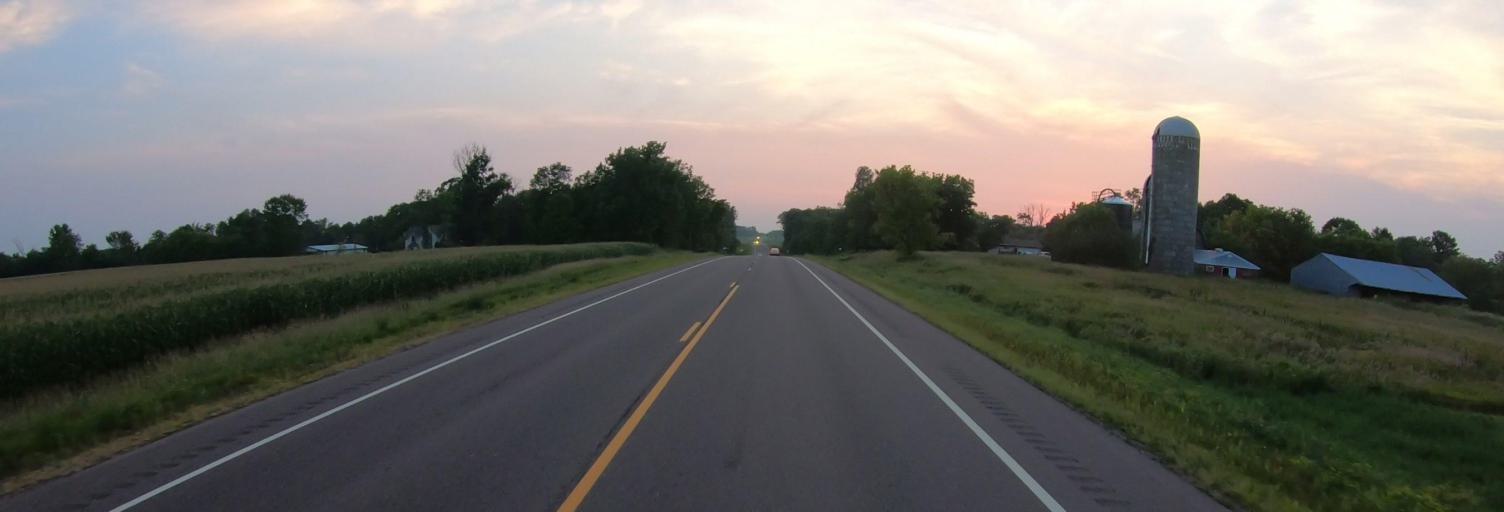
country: US
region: Minnesota
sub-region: Pine County
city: Rock Creek
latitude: 45.7735
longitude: -92.9152
